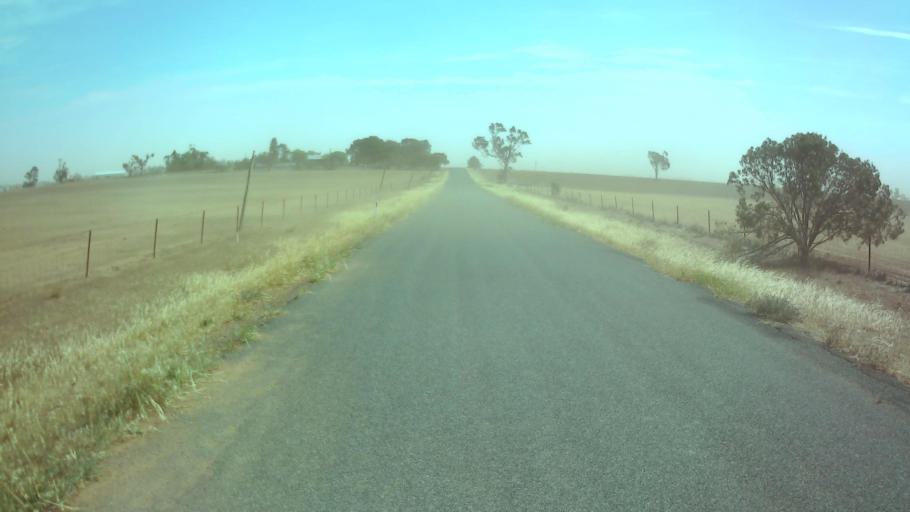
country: AU
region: New South Wales
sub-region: Weddin
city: Grenfell
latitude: -33.7339
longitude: 147.9974
